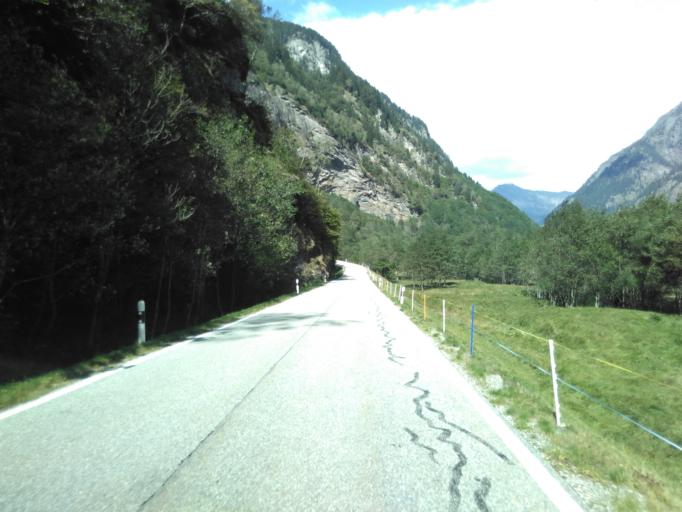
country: CH
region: Grisons
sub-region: Moesa District
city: Cauco
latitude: 46.3407
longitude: 9.1195
